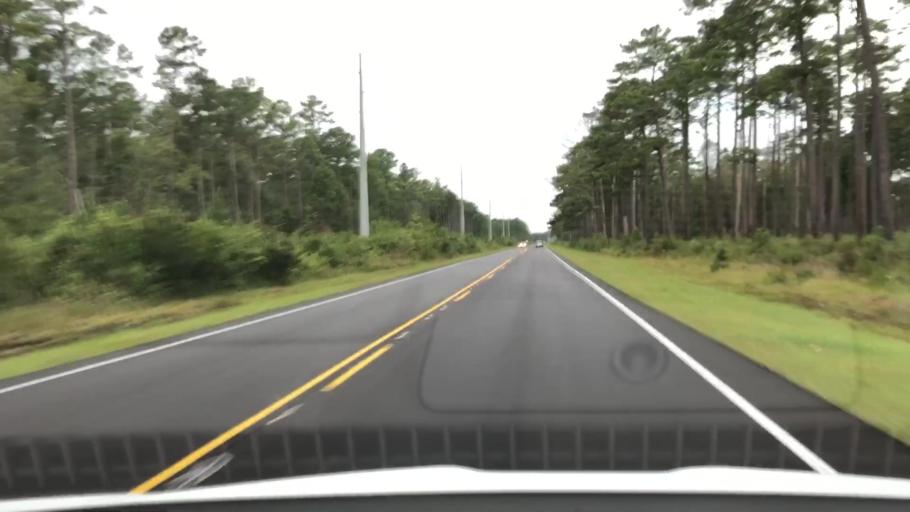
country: US
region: North Carolina
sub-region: Onslow County
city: Swansboro
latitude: 34.7765
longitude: -77.1017
